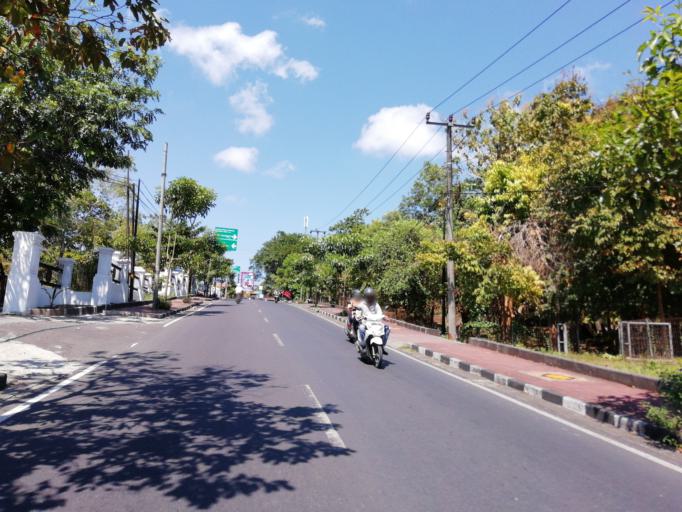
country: ID
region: Bali
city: Jimbaran
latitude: -8.7988
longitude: 115.1710
